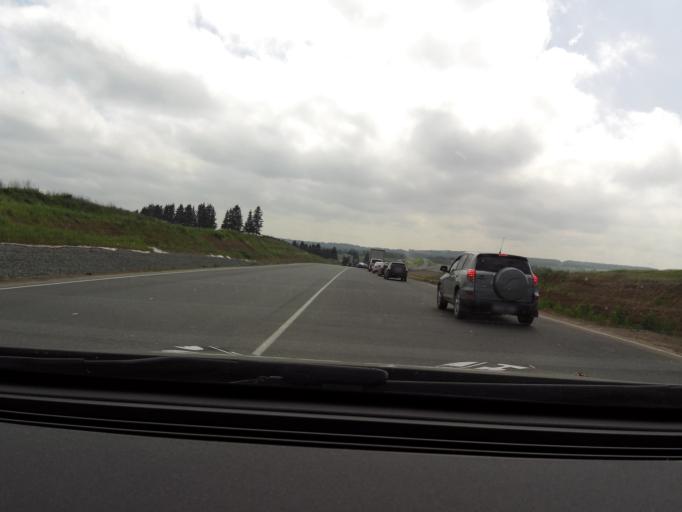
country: RU
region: Perm
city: Zvezdnyy
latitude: 57.7904
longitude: 56.3375
